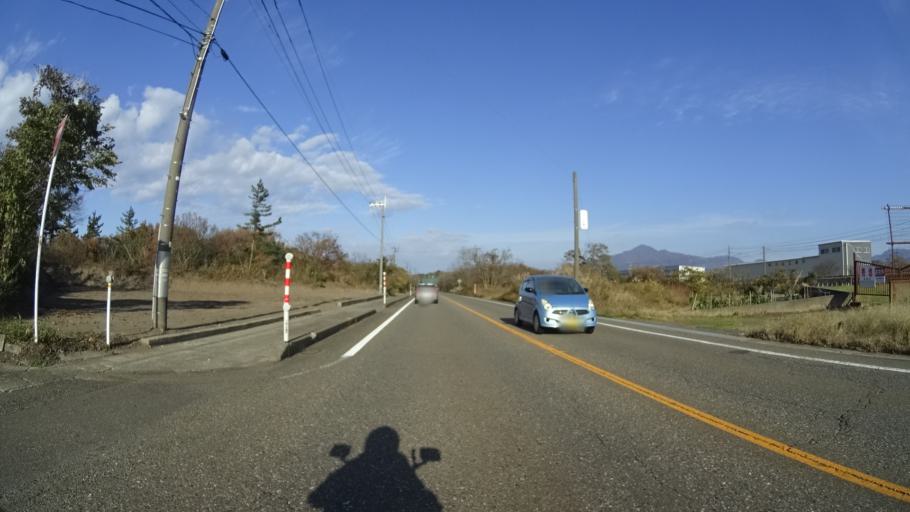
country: JP
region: Niigata
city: Joetsu
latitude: 37.2597
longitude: 138.3694
